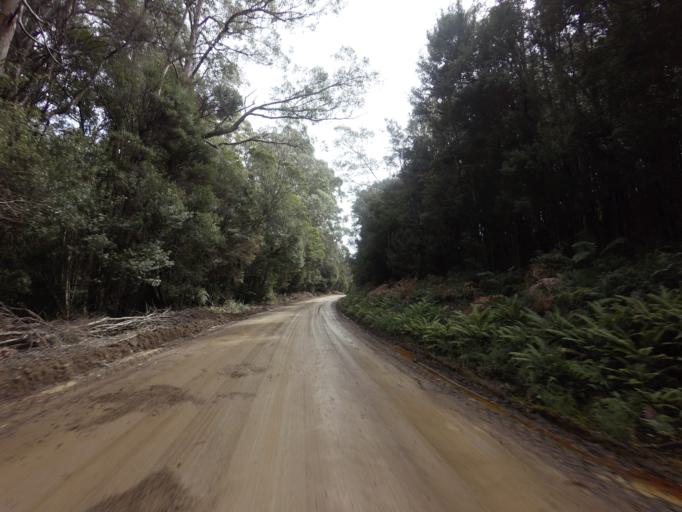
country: AU
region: Tasmania
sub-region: Huon Valley
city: Geeveston
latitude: -43.4074
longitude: 146.8692
